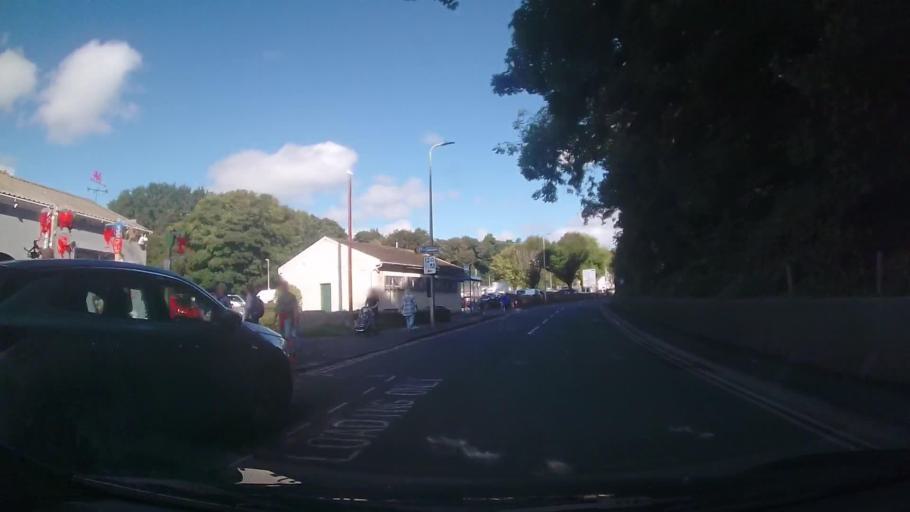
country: GB
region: Wales
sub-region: Pembrokeshire
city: Tenby
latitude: 51.6728
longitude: -4.7080
